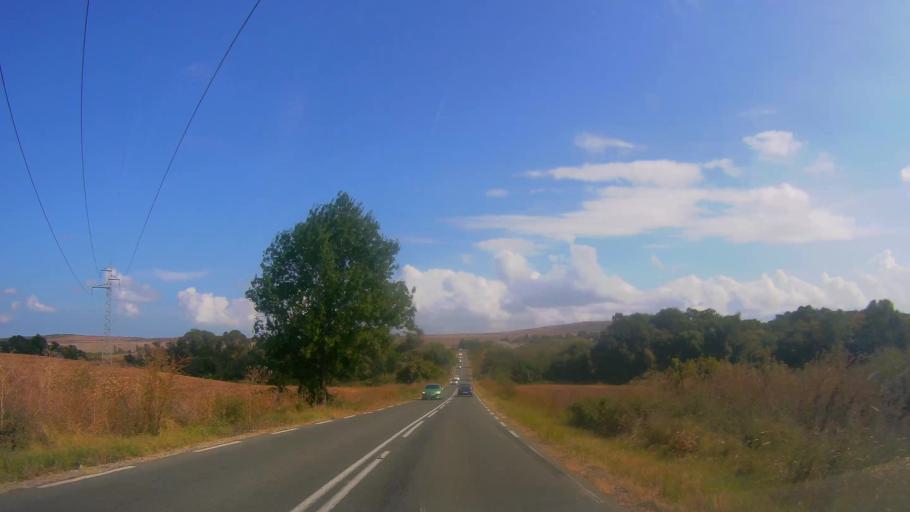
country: BG
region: Burgas
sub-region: Obshtina Burgas
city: Burgas
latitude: 42.4766
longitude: 27.3559
